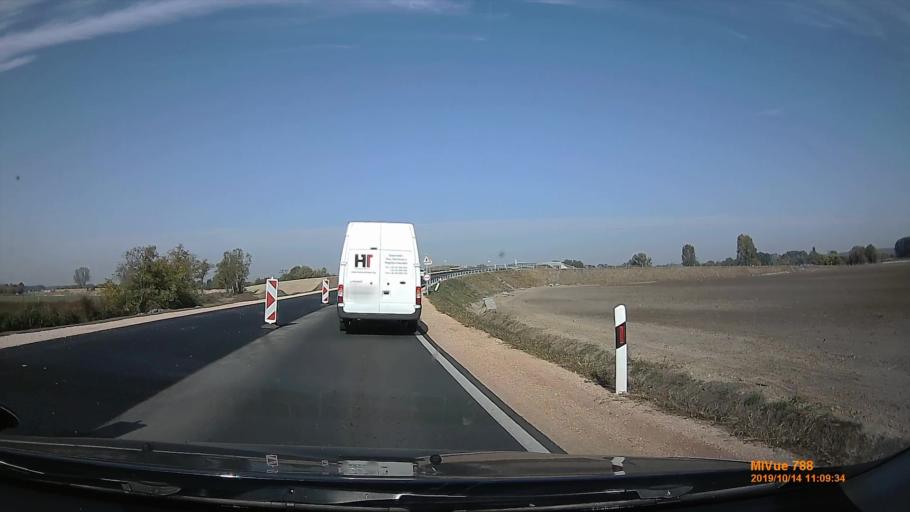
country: HU
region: Pest
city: Peteri
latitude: 47.3689
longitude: 19.4233
